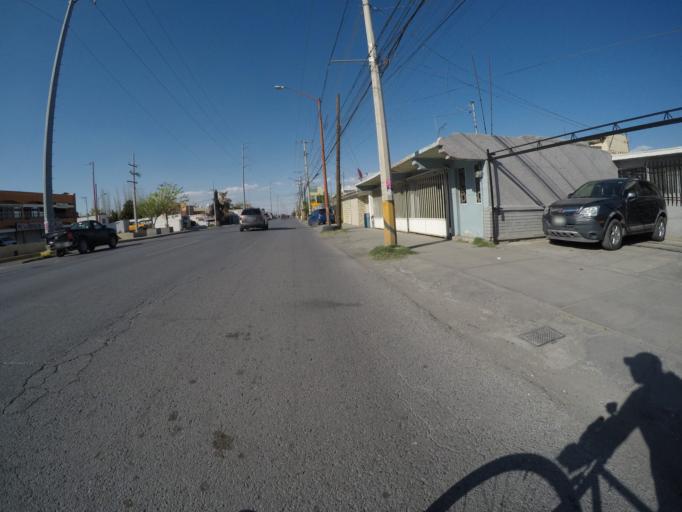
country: MX
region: Chihuahua
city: Ciudad Juarez
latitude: 31.7224
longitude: -106.4430
